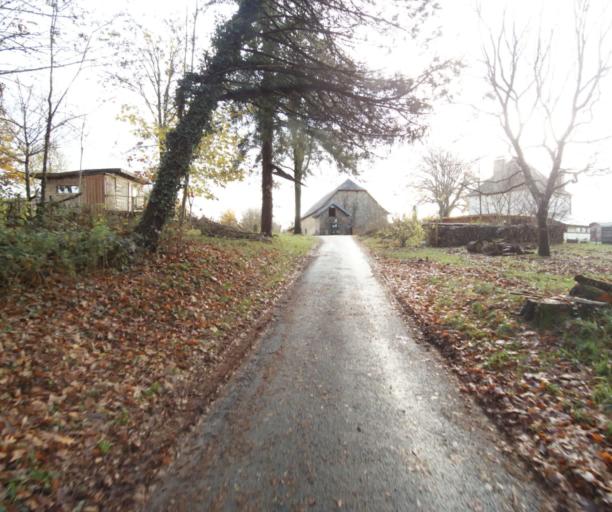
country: FR
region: Limousin
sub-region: Departement de la Correze
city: Cornil
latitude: 45.2235
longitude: 1.6750
